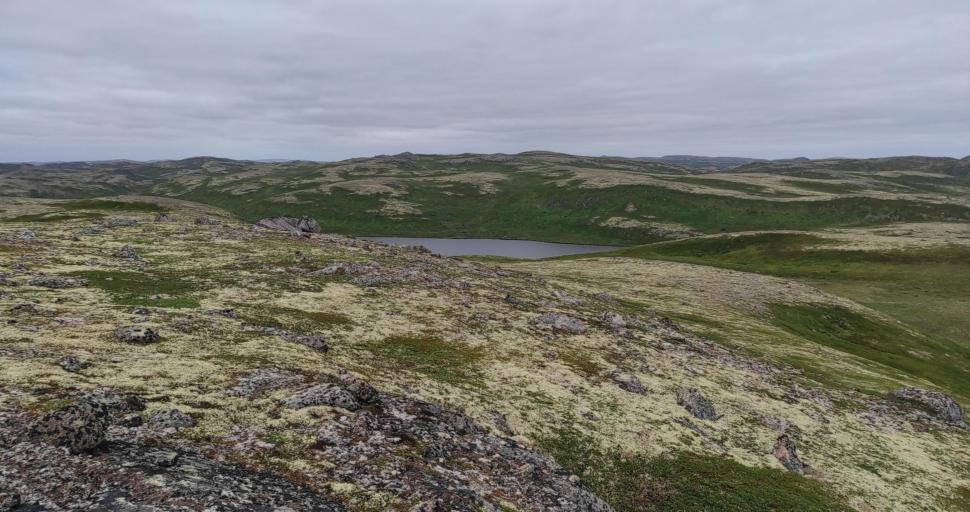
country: RU
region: Murmansk
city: Teriberka
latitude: 69.2006
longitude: 35.3586
